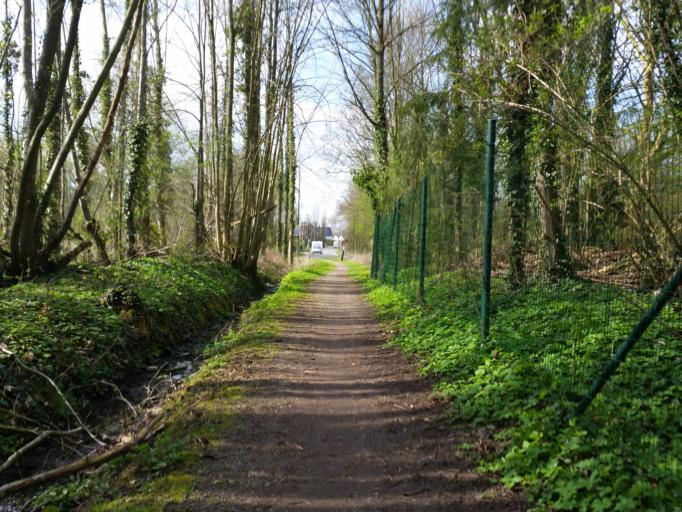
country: BE
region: Flanders
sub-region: Provincie Vlaams-Brabant
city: Kampenhout
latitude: 50.9277
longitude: 4.5507
